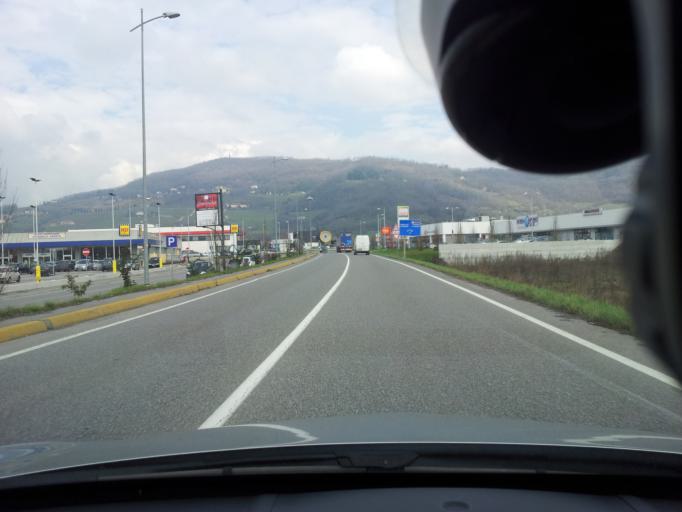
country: IT
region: Lombardy
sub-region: Provincia di Bergamo
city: Grumello del Monte
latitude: 45.6357
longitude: 9.8855
